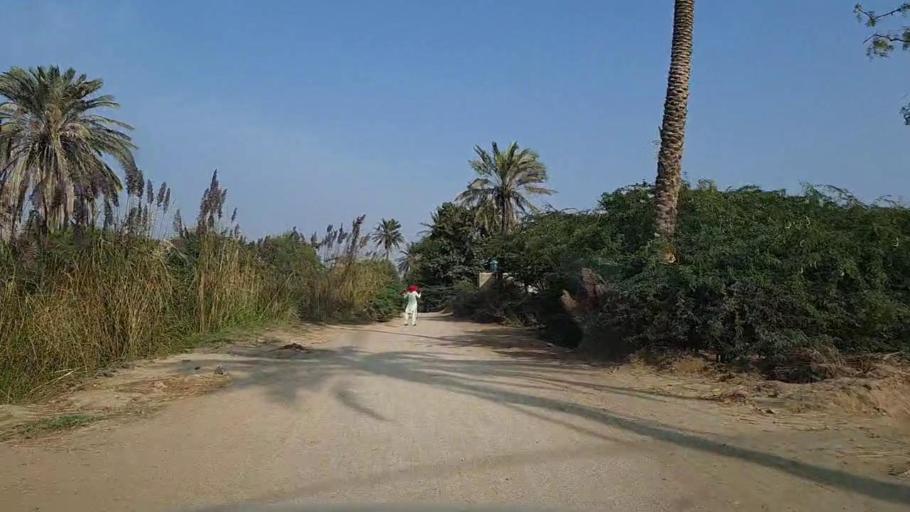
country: PK
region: Sindh
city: Mirpur Sakro
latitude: 24.5929
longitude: 67.6078
